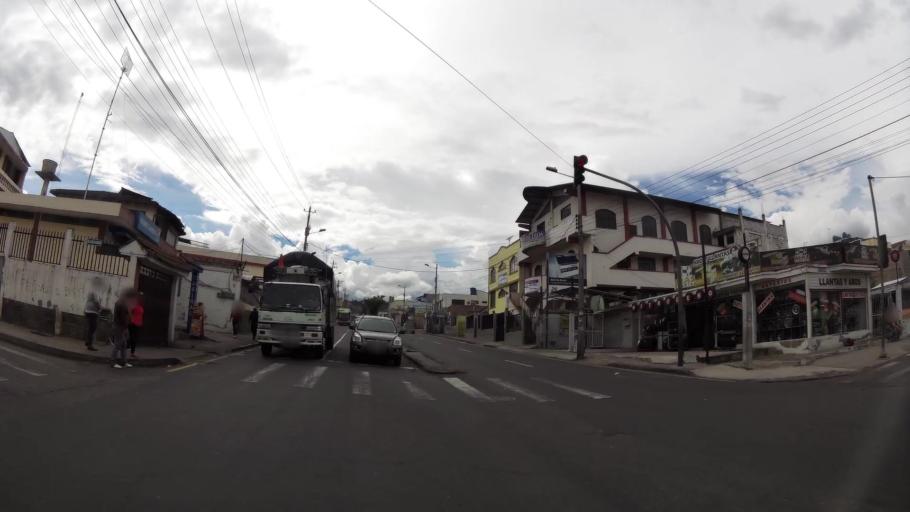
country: EC
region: Tungurahua
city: Ambato
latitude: -1.2759
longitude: -78.6273
